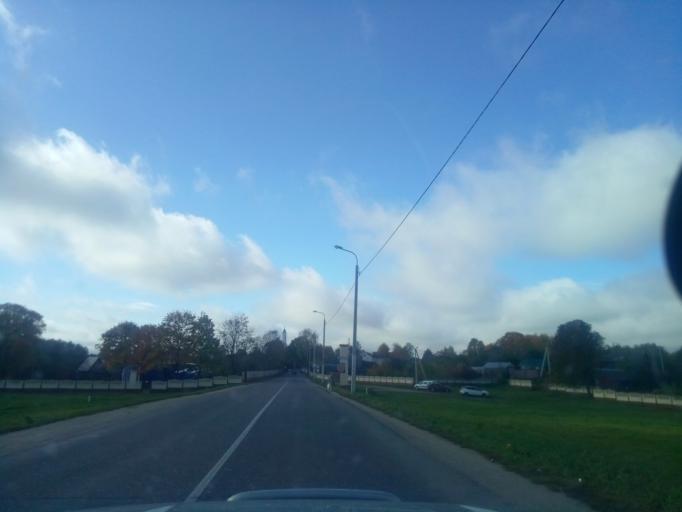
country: BY
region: Minsk
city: Zaslawye
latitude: 54.0060
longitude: 27.2999
